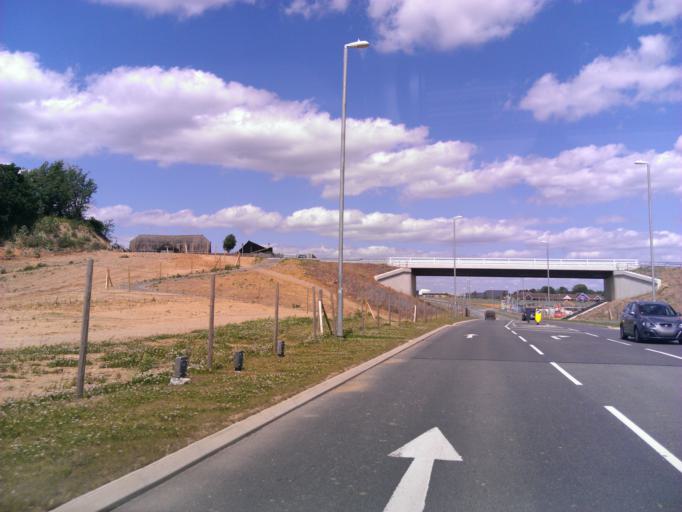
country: GB
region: England
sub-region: Essex
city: Eight Ash Green
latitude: 51.8789
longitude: 0.8267
